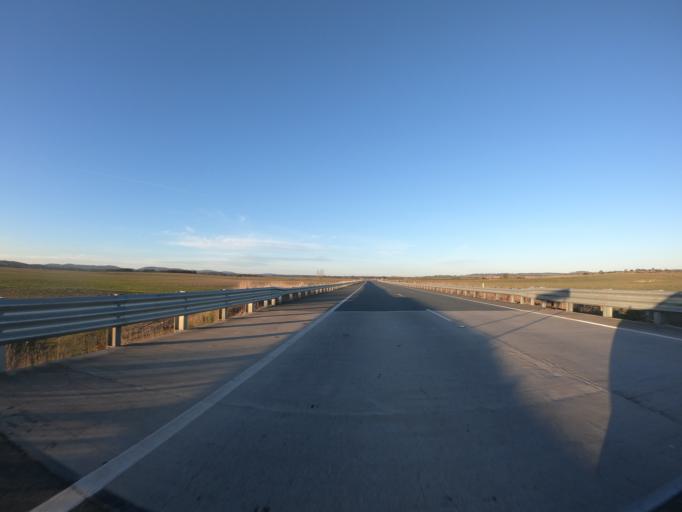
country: AU
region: New South Wales
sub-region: Goulburn Mulwaree
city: Goulburn
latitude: -34.8499
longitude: 149.5556
